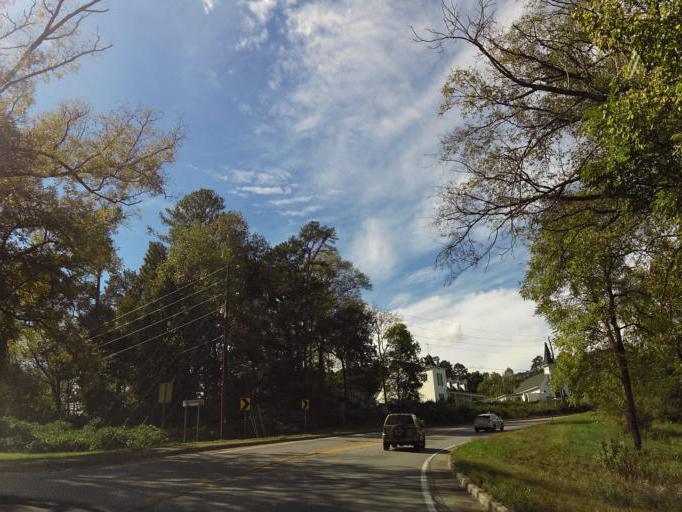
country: US
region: Georgia
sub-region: Pickens County
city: Nelson
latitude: 34.4136
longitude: -84.3740
